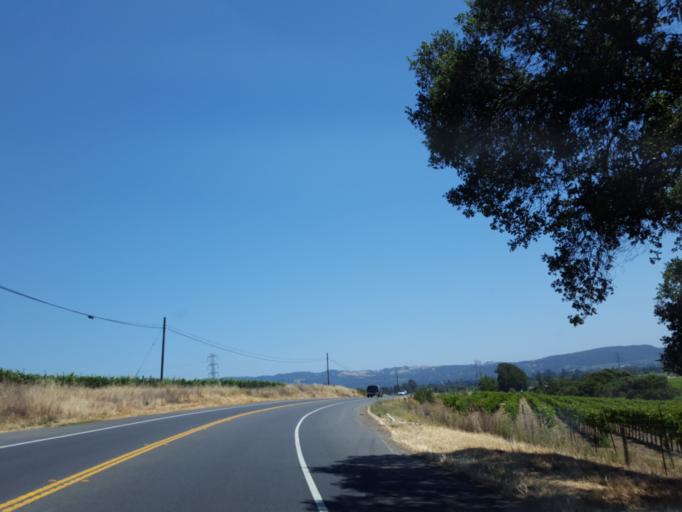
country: US
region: California
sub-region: Sonoma County
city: Temelec
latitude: 38.2478
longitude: -122.5001
